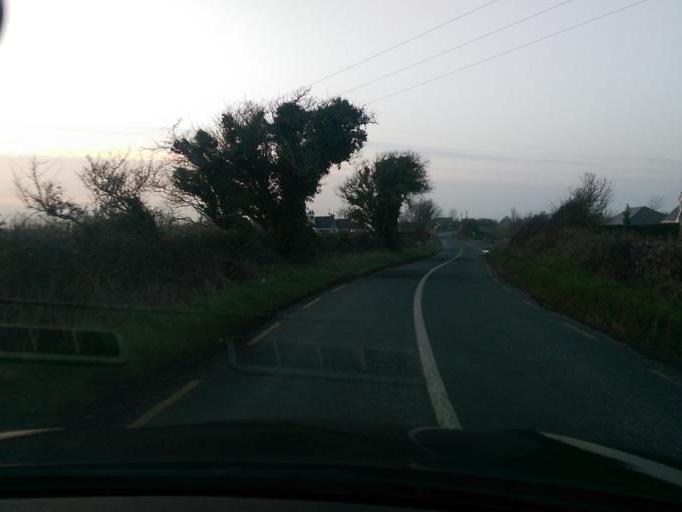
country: IE
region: Connaught
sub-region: County Galway
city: Athenry
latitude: 53.2654
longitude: -8.6887
